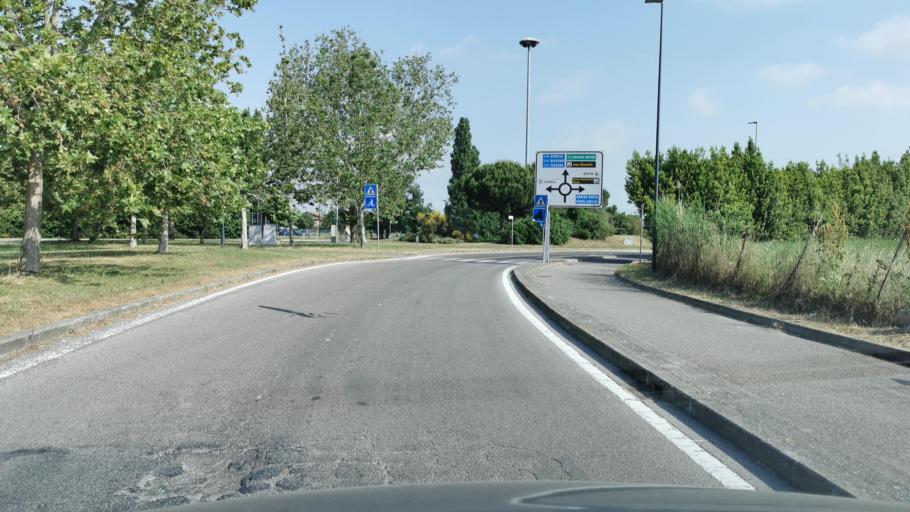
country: IT
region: Emilia-Romagna
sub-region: Provincia di Ravenna
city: Ravenna
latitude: 44.4264
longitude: 12.2159
